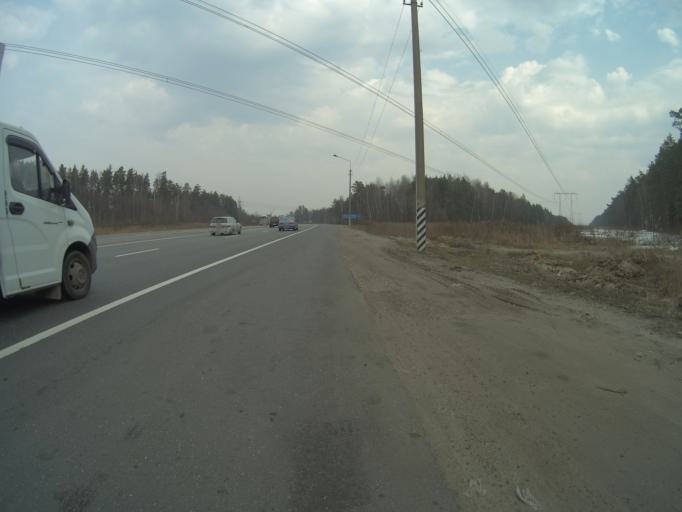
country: RU
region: Vladimir
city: Kommunar
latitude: 56.0586
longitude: 40.4471
